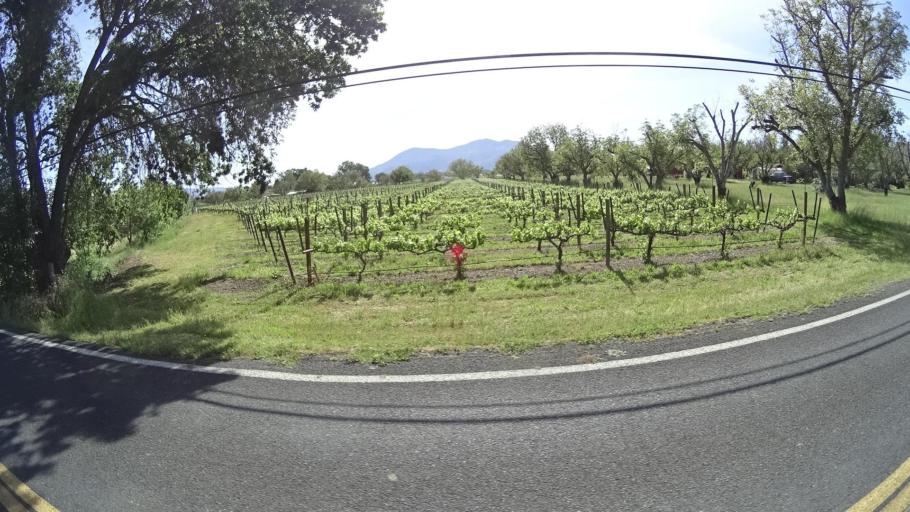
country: US
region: California
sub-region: Lake County
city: Kelseyville
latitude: 38.9813
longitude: -122.8943
